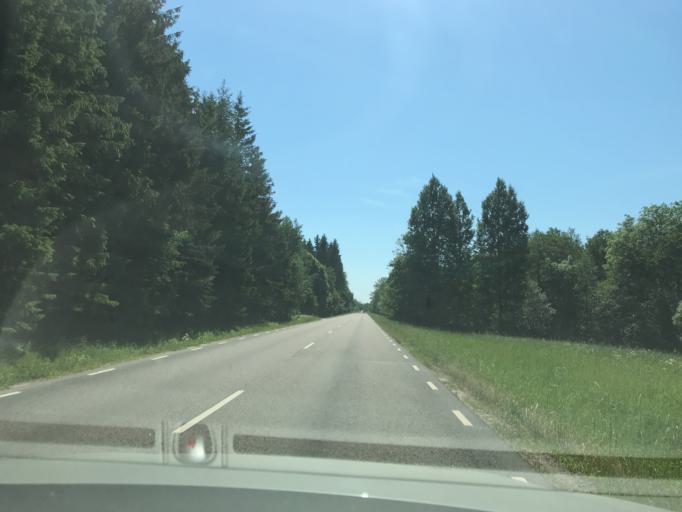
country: SE
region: Vaestra Goetaland
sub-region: Gotene Kommun
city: Kallby
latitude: 58.5932
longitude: 13.3827
